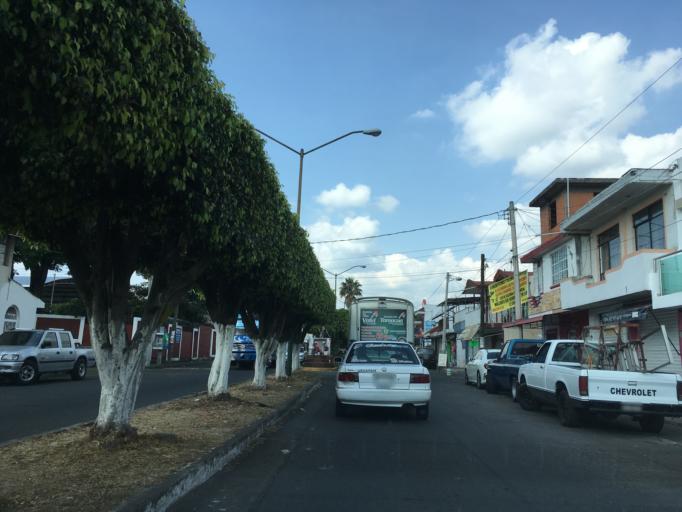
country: MX
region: Michoacan
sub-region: Uruapan
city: Uruapan
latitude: 19.3945
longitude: -102.0518
